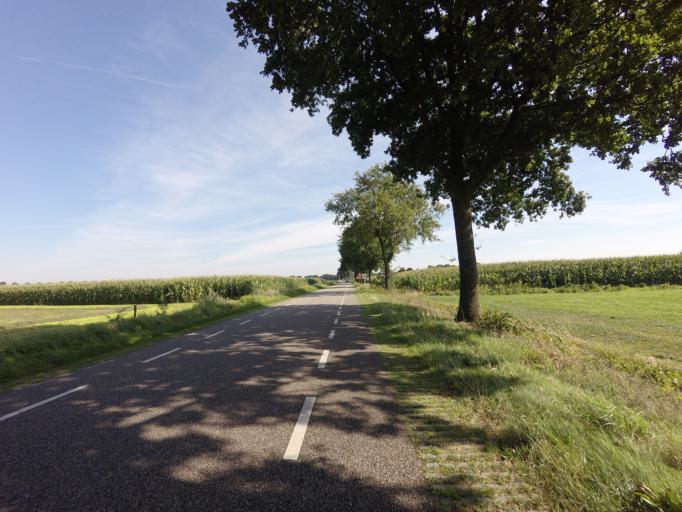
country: NL
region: Gelderland
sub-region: Oost Gelre
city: Lichtenvoorde
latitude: 52.0337
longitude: 6.5379
